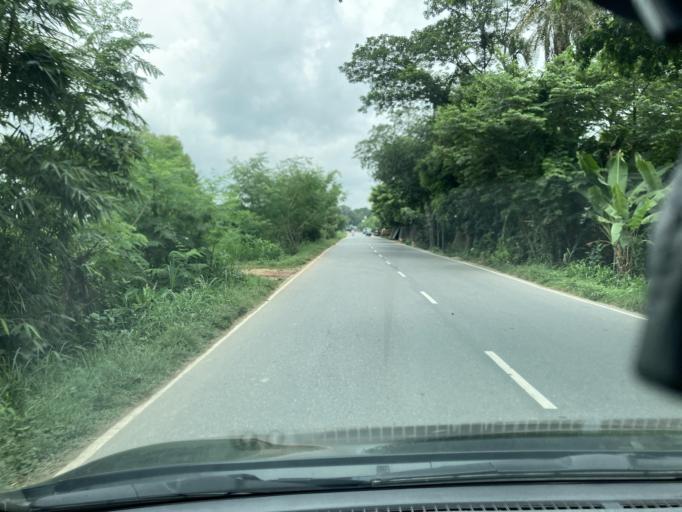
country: BD
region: Dhaka
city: Azimpur
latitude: 23.8061
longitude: 90.2054
